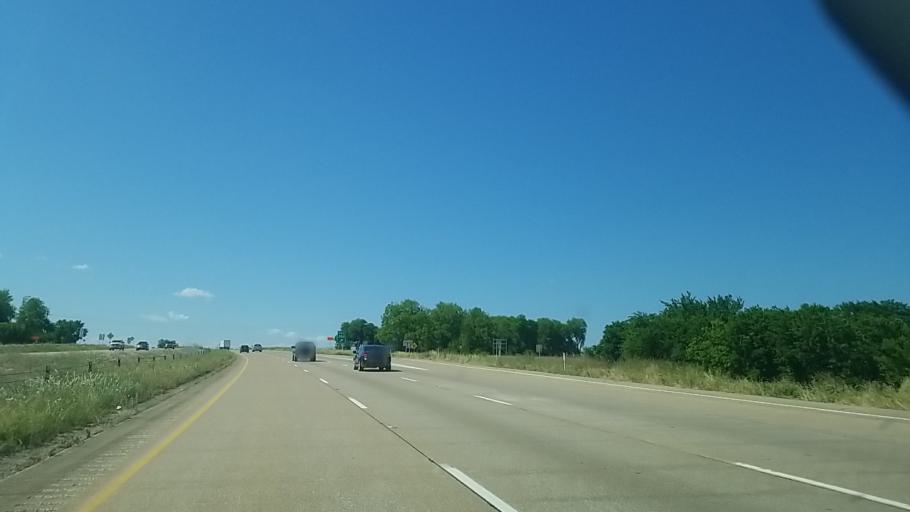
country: US
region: Texas
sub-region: Ellis County
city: Palmer
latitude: 32.4728
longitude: -96.6609
